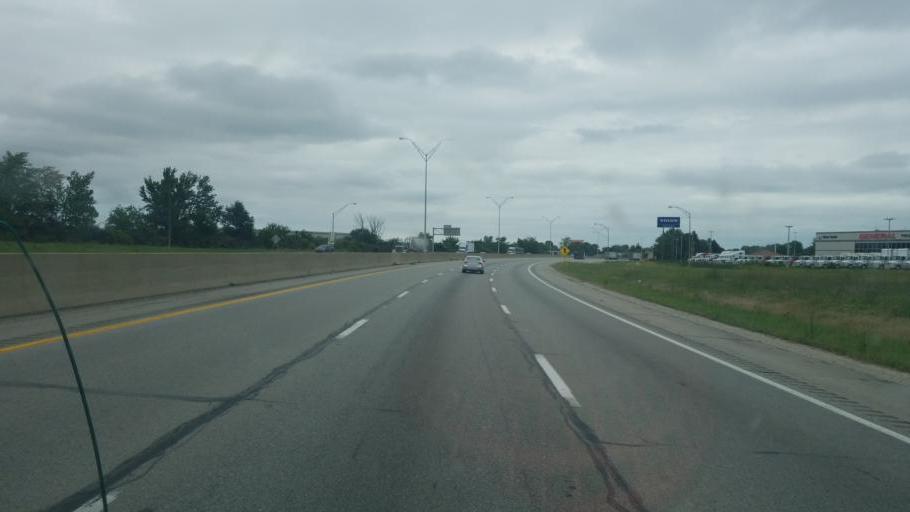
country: US
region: Ohio
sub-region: Lucas County
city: Oregon
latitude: 41.7223
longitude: -83.5005
